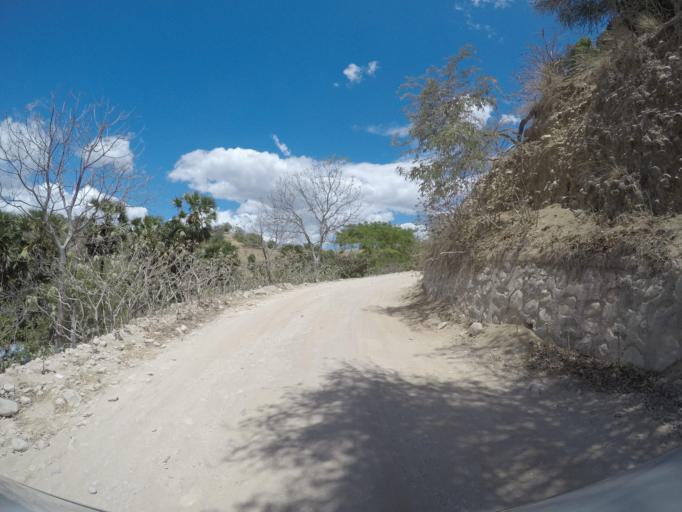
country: TL
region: Baucau
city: Baucau
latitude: -8.4734
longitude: 126.6024
